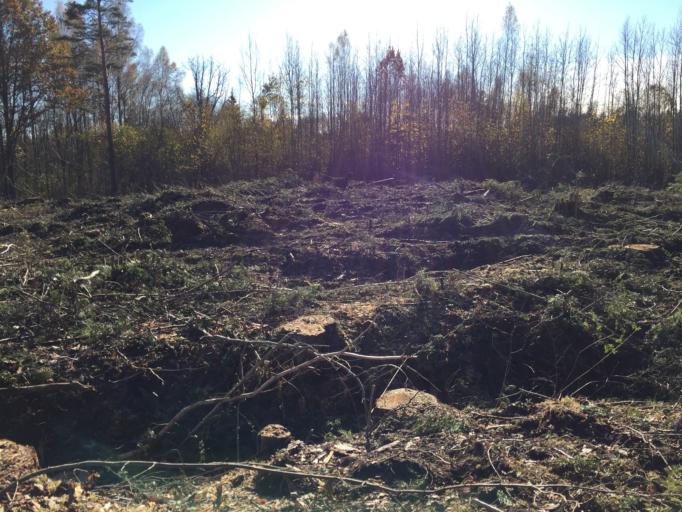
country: LV
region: Skriveri
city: Skriveri
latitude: 56.5923
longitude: 25.1729
